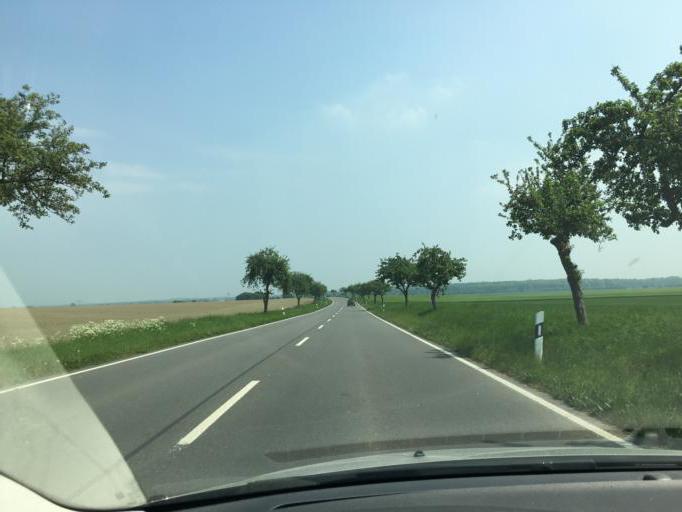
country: DE
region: Saxony
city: Belgershain
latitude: 51.2679
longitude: 12.5387
